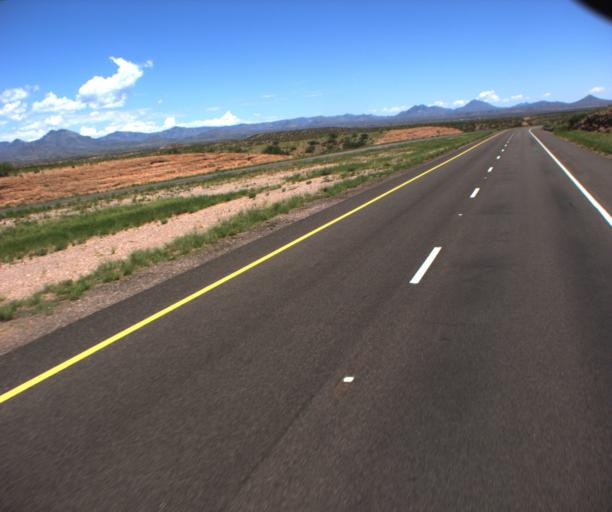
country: US
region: Arizona
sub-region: Greenlee County
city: Clifton
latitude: 32.9784
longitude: -109.2518
